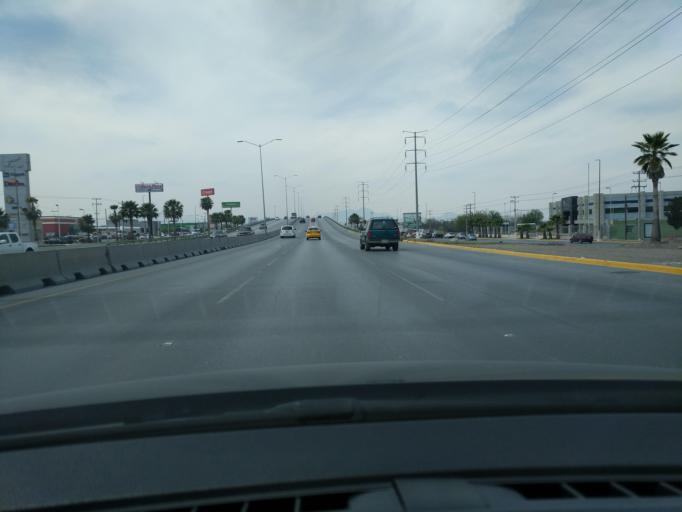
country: MX
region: Coahuila
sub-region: Arteaga
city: Arteaga
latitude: 25.4341
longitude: -100.9225
